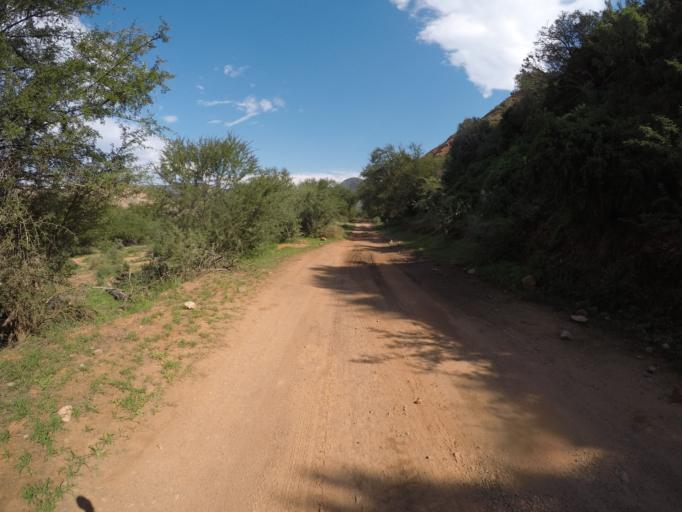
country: ZA
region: Eastern Cape
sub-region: Cacadu District Municipality
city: Kareedouw
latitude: -33.6619
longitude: 24.3939
